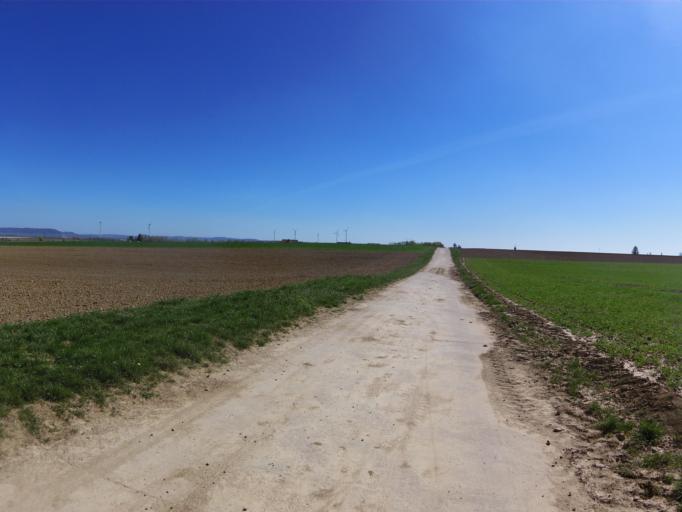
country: DE
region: Bavaria
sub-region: Regierungsbezirk Unterfranken
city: Biebelried
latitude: 49.8030
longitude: 10.0861
